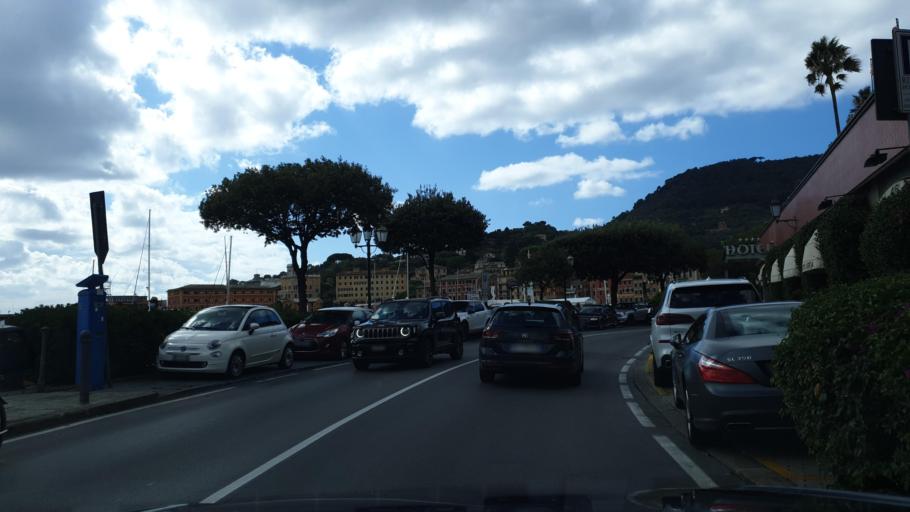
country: IT
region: Liguria
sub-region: Provincia di Genova
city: Santa Margherita Ligure
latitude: 44.3323
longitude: 9.2141
